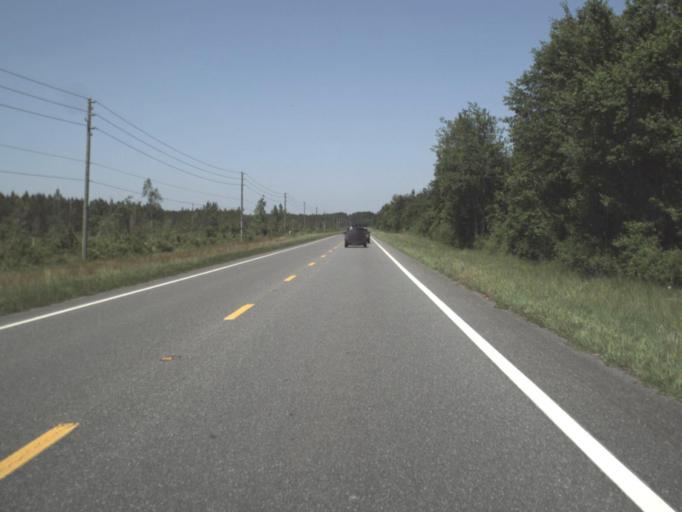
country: US
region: Florida
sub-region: Columbia County
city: Watertown
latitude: 30.2013
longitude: -82.4621
